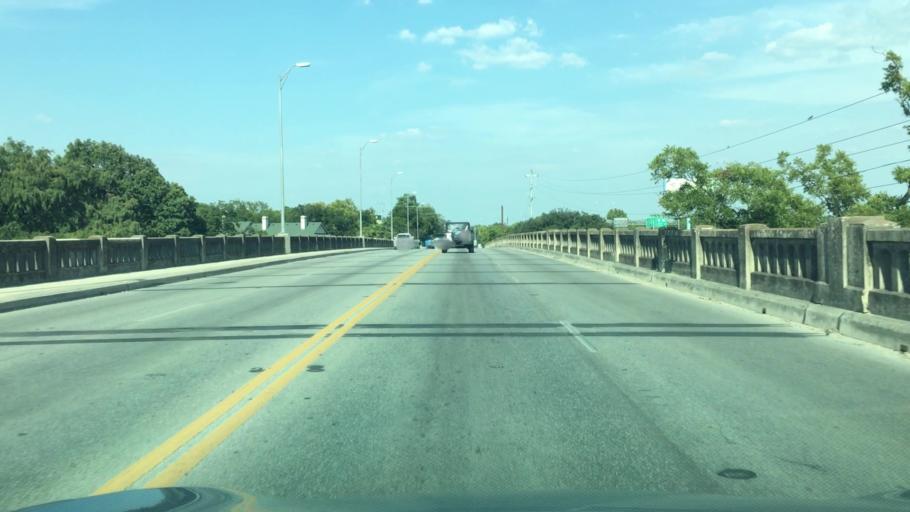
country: US
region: Texas
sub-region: Comal County
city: New Braunfels
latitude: 29.6942
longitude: -98.1078
